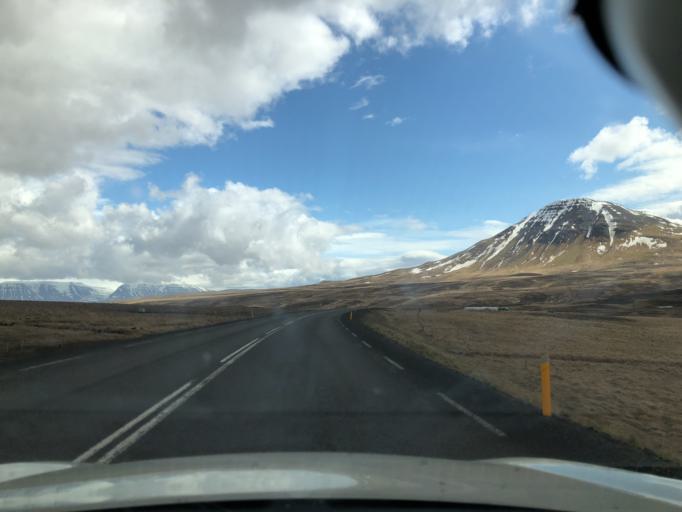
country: IS
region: Northwest
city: Saudarkrokur
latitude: 65.5198
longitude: -19.6140
